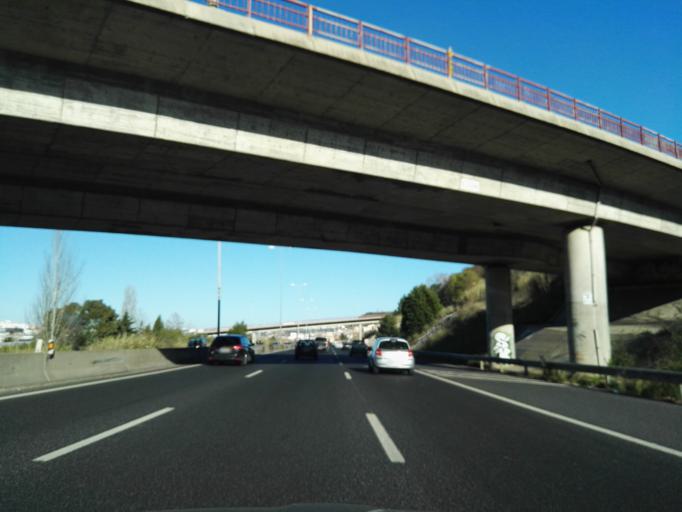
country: PT
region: Lisbon
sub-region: Odivelas
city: Pontinha
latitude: 38.7718
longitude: -9.2030
